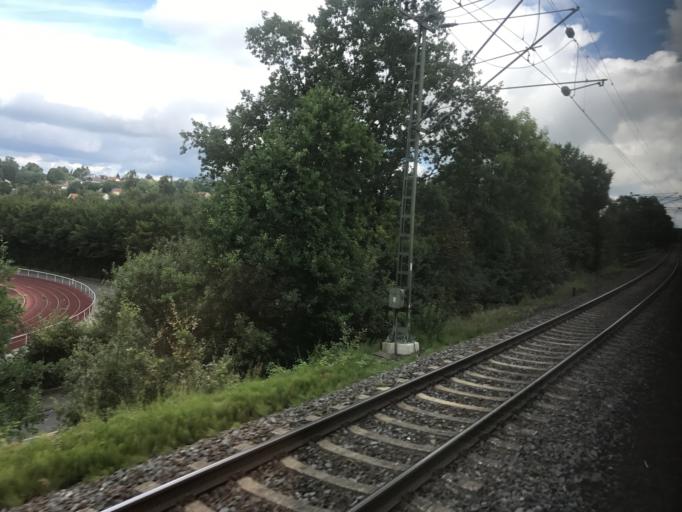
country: DE
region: Hesse
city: Schwalmstadt
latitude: 50.9135
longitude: 9.1932
